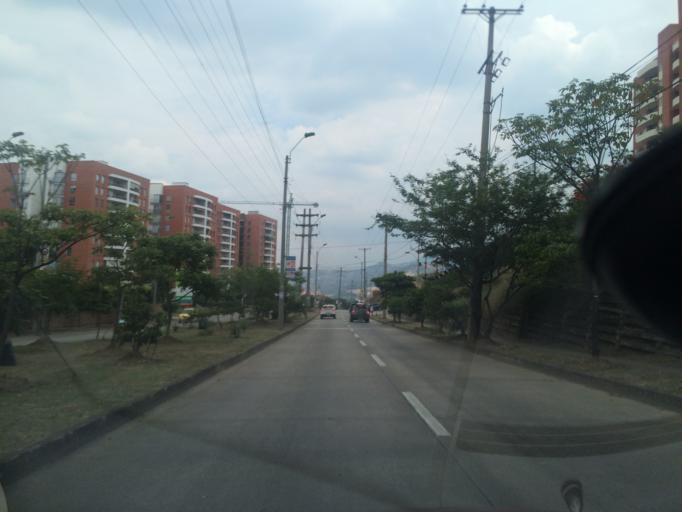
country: CO
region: Valle del Cauca
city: Cali
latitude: 3.4319
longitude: -76.5513
